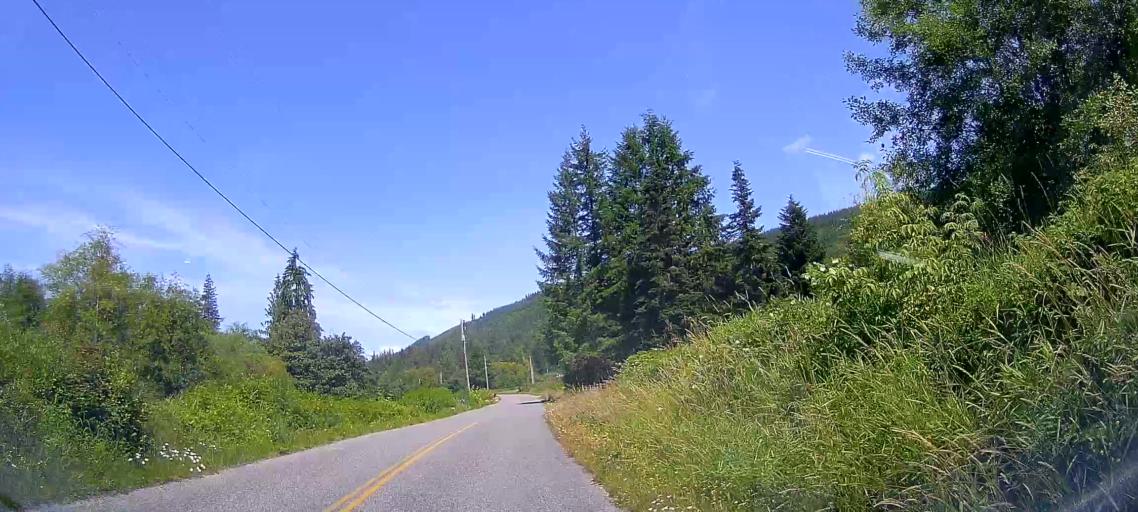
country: US
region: Washington
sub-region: Whatcom County
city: Sudden Valley
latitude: 48.6236
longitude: -122.3209
